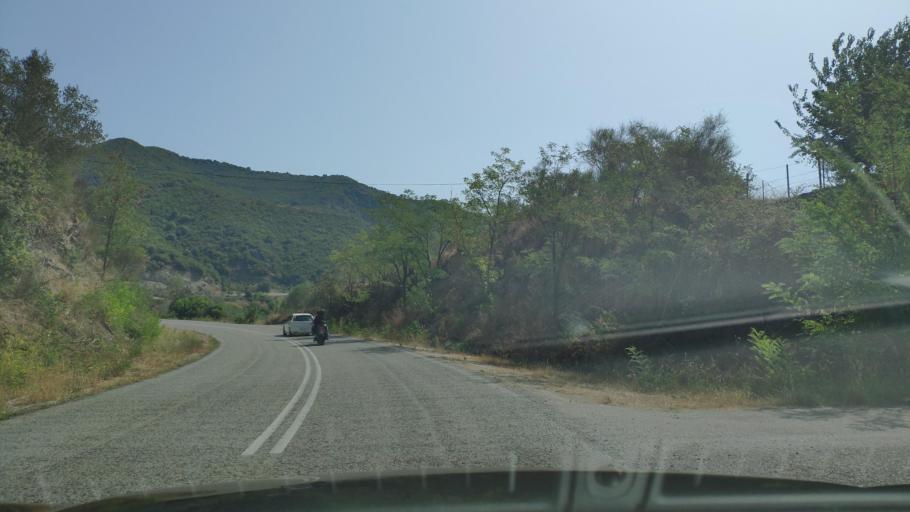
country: GR
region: Epirus
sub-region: Nomos Artas
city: Peta
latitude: 39.1679
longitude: 21.0538
